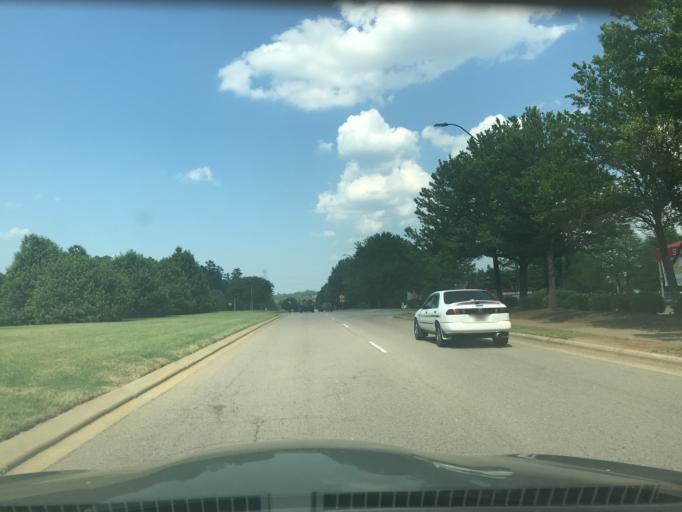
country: US
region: North Carolina
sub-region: Wake County
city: Wake Forest
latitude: 35.9413
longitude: -78.5618
